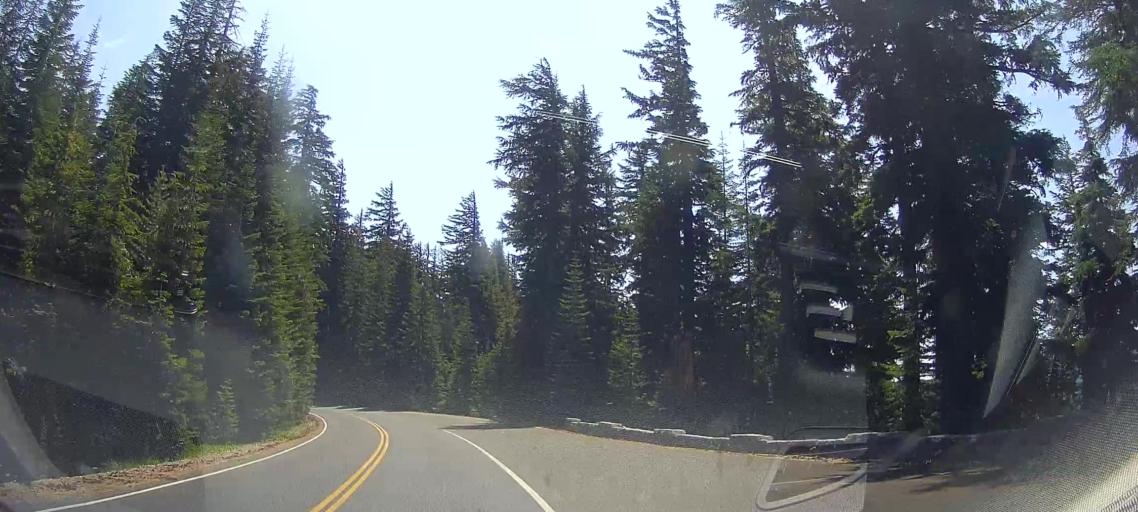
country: US
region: Oregon
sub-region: Jackson County
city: Shady Cove
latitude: 42.9771
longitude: -122.1058
